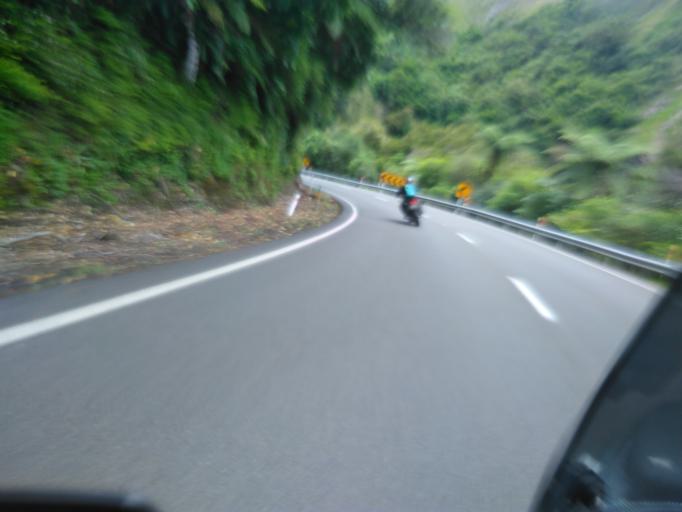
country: NZ
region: Bay of Plenty
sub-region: Opotiki District
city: Opotiki
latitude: -38.2685
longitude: 177.3063
